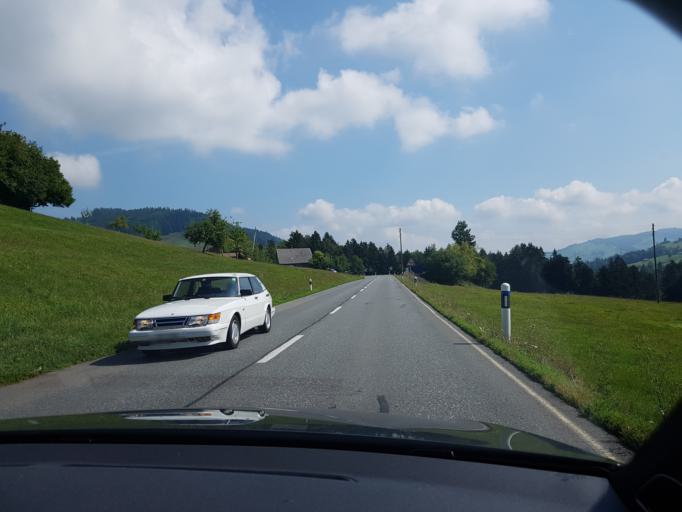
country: CH
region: Saint Gallen
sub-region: Wahlkreis See-Gaster
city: Gommiswald
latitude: 47.2690
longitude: 9.0530
